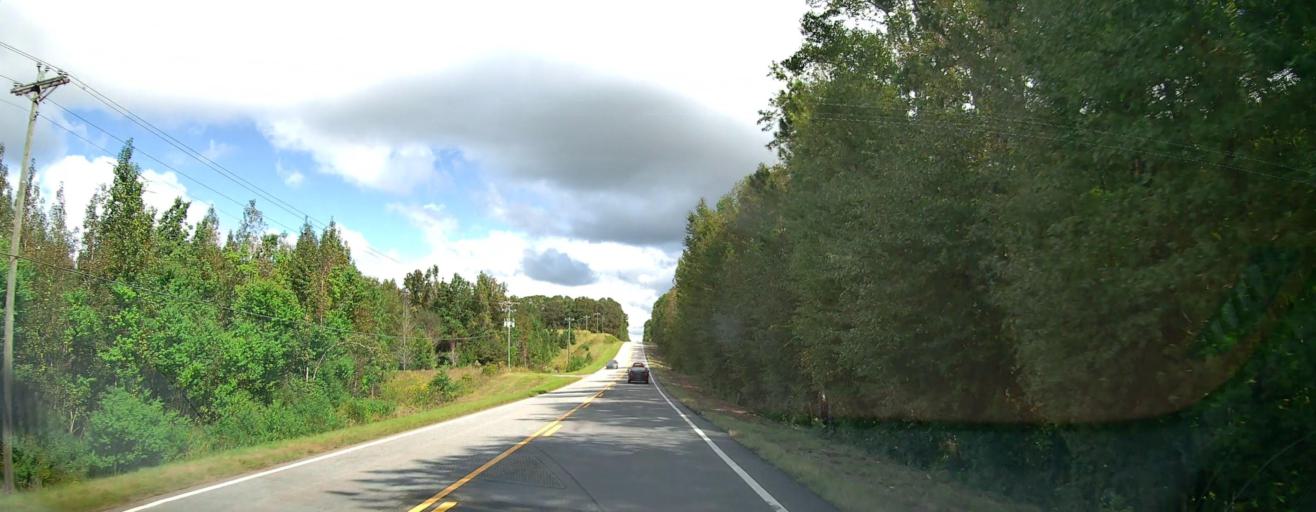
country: US
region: Georgia
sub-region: Jones County
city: Gray
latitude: 32.9565
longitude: -83.4457
